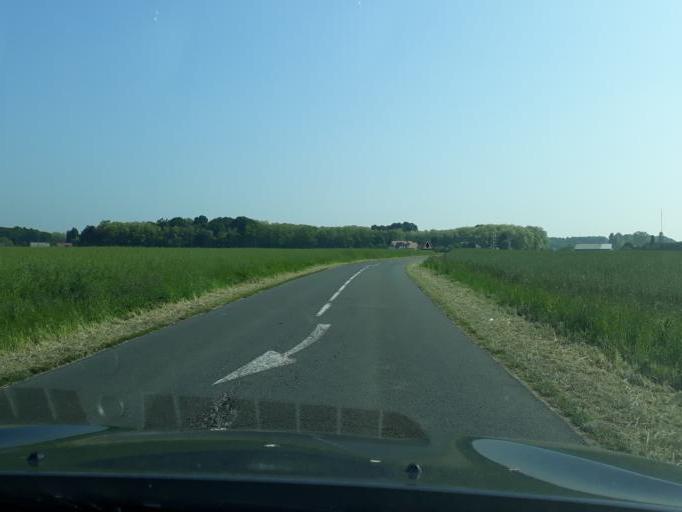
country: FR
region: Centre
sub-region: Departement du Loiret
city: Vennecy
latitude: 47.9500
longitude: 2.0702
